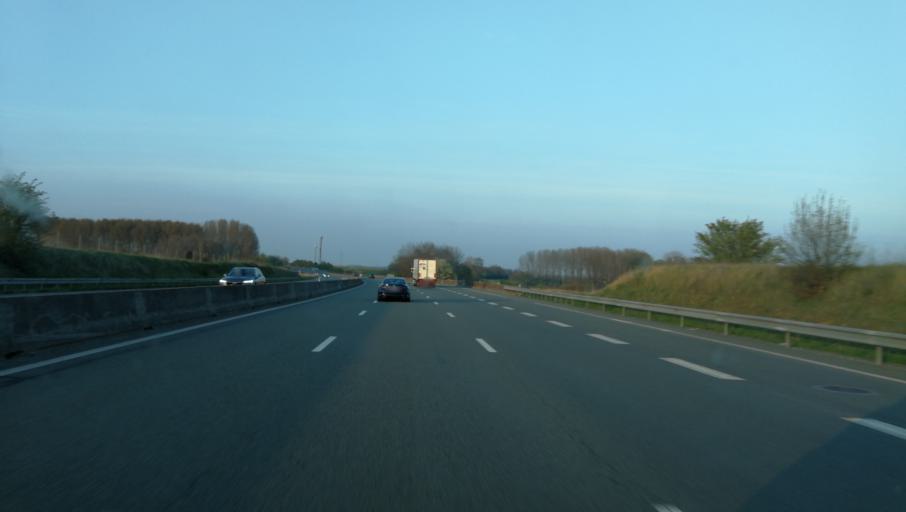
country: FR
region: Centre
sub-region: Departement d'Eure-et-Loir
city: Morancez
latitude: 48.3798
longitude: 1.4824
